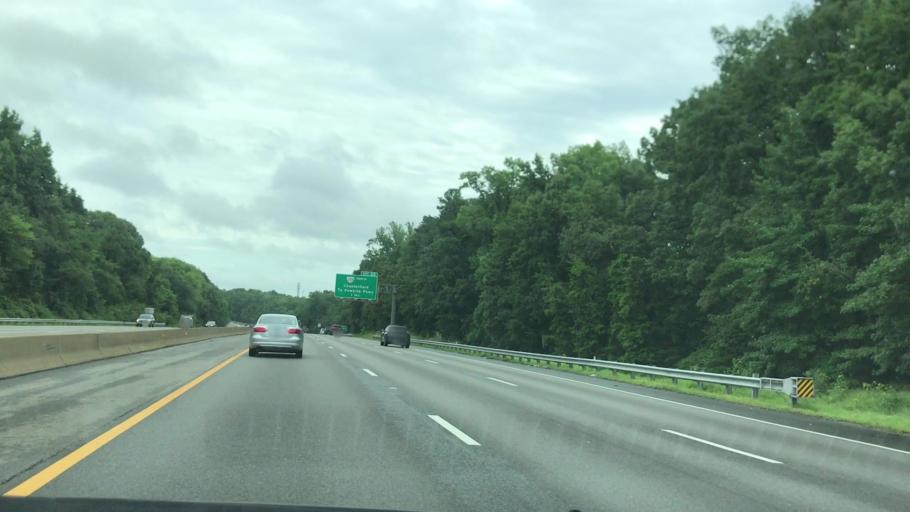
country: US
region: Virginia
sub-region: Chesterfield County
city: Chester
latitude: 37.3608
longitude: -77.4038
